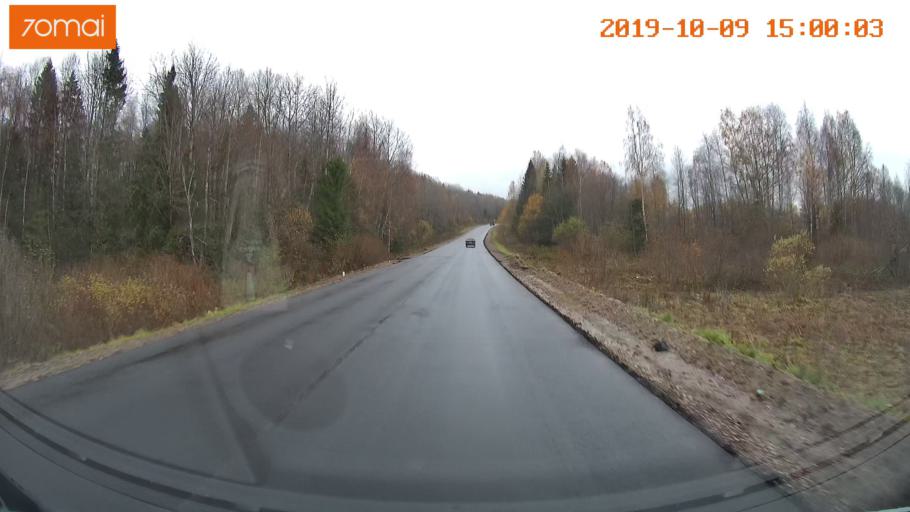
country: RU
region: Kostroma
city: Chistyye Bory
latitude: 58.3136
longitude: 41.6750
